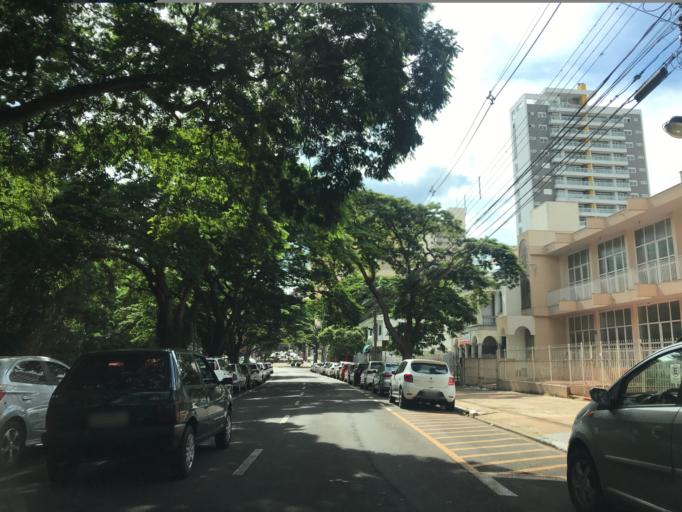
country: BR
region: Parana
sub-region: Maringa
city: Maringa
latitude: -23.4229
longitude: -51.9297
